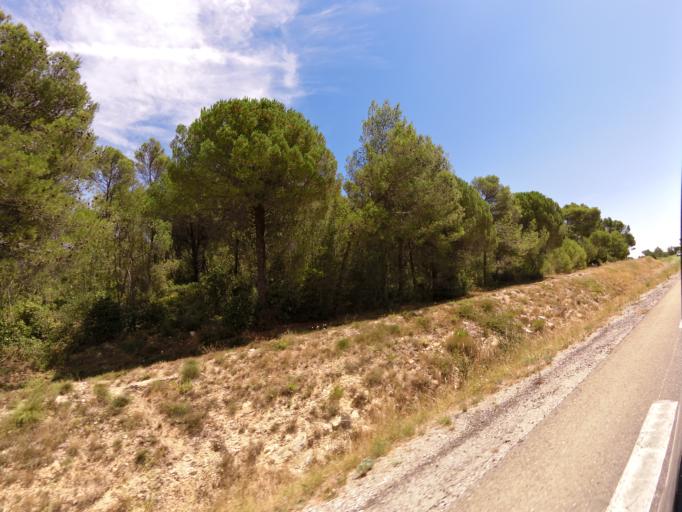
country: FR
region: Languedoc-Roussillon
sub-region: Departement du Gard
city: Aubais
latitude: 43.7789
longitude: 4.1385
